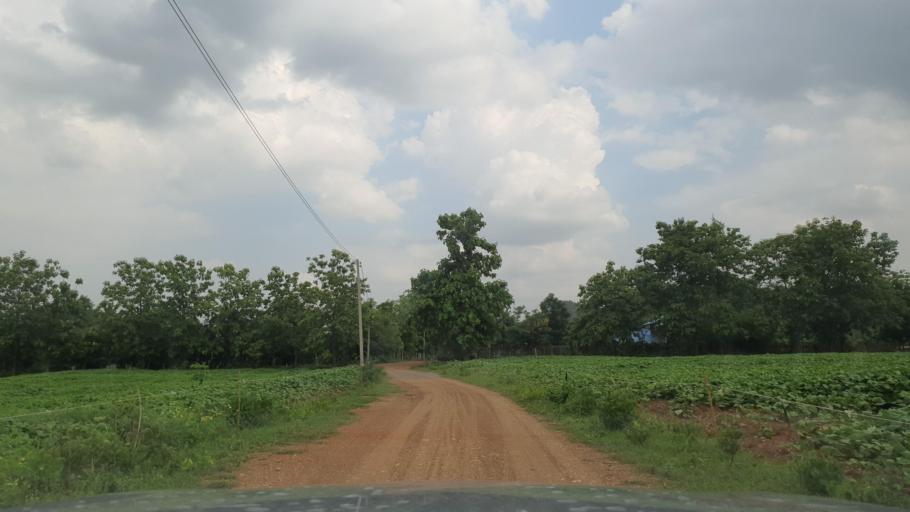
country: TH
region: Sukhothai
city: Thung Saliam
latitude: 17.2469
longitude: 99.5438
